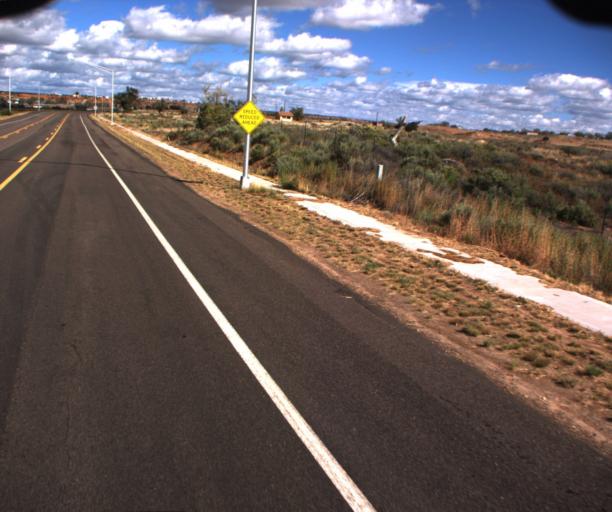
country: US
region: Arizona
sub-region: Apache County
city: Houck
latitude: 35.2012
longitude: -109.3327
